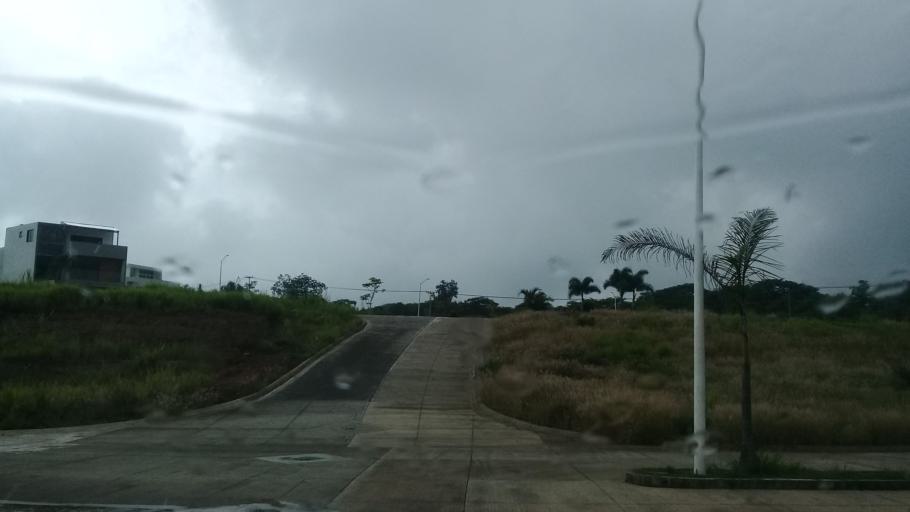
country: MX
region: Veracruz
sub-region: Emiliano Zapata
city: Jacarandas
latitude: 19.5061
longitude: -96.8466
